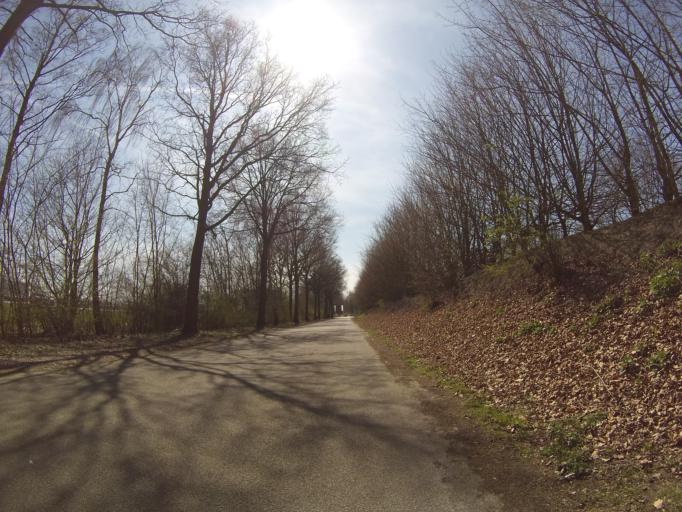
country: NL
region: Gelderland
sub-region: Gemeente Ermelo
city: Horst
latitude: 52.2728
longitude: 5.5391
